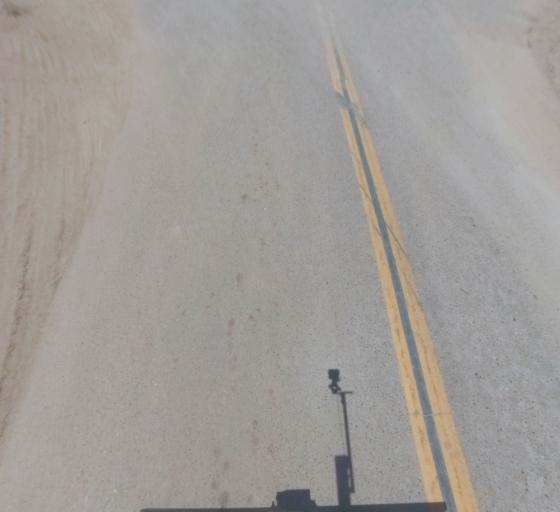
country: US
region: California
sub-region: Madera County
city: Parkwood
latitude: 36.8585
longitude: -120.1463
